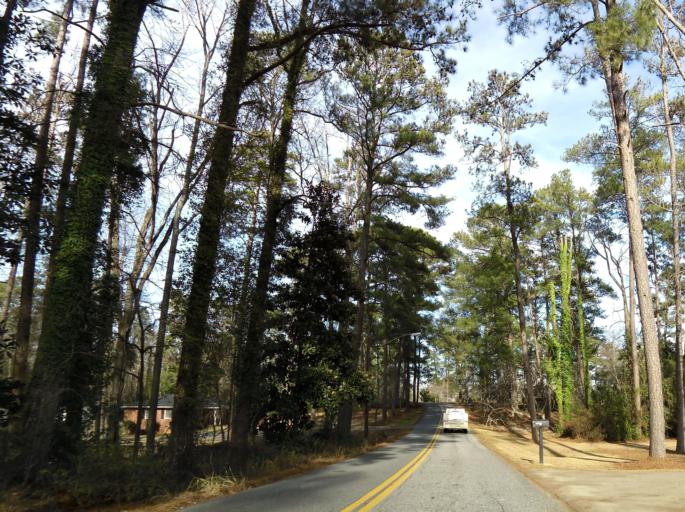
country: US
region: Georgia
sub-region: Bibb County
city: Macon
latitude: 32.8756
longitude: -83.7065
